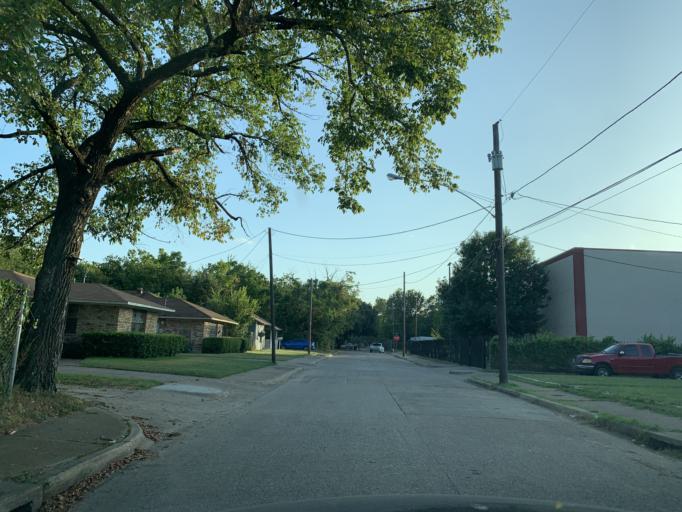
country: US
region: Texas
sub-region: Dallas County
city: Dallas
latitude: 32.7537
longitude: -96.7593
